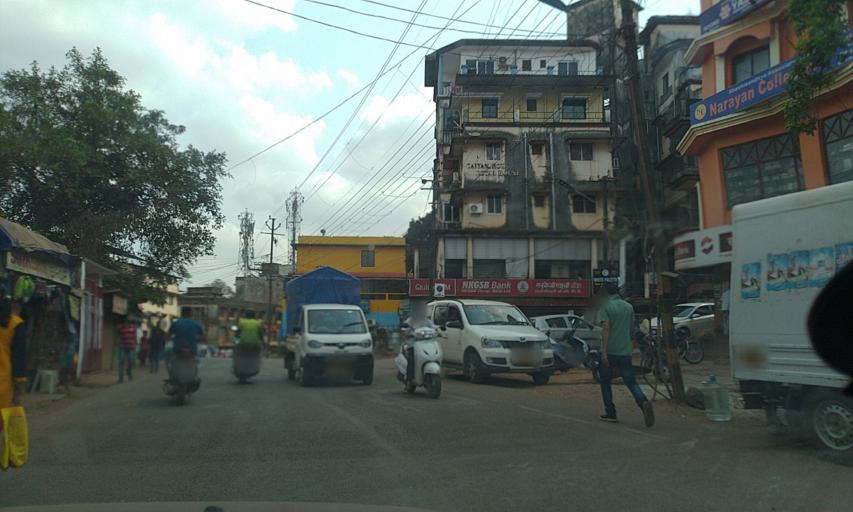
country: IN
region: Goa
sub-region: North Goa
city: Ponda
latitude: 15.4007
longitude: 74.0057
